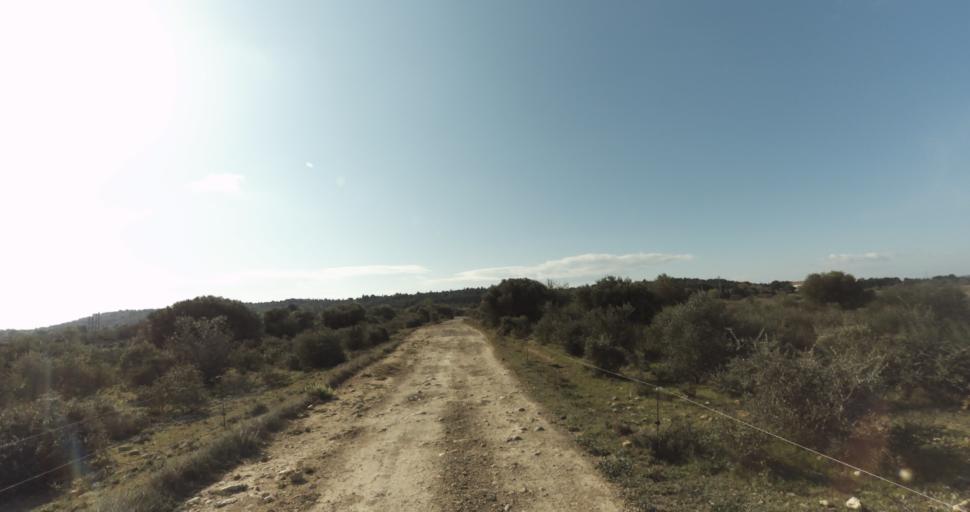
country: FR
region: Languedoc-Roussillon
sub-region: Departement de l'Aude
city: Leucate
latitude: 42.9376
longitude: 3.0126
